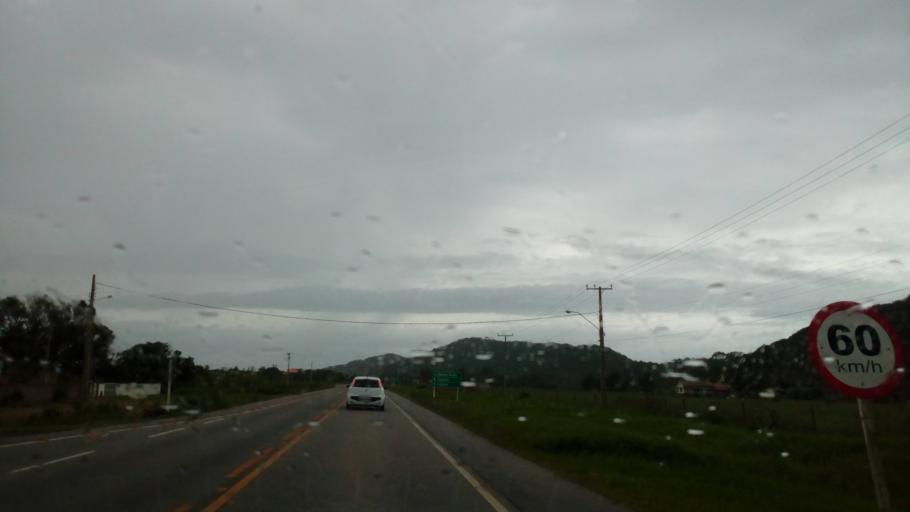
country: BR
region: Santa Catarina
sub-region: Laguna
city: Laguna
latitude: -28.5290
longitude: -48.7792
